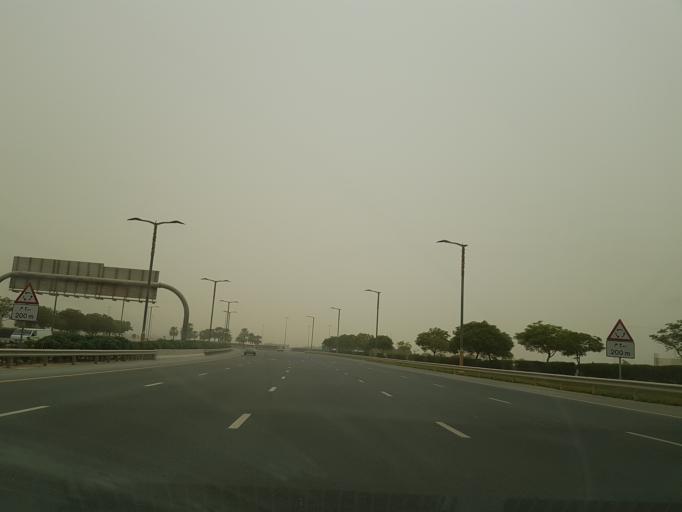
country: AE
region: Dubai
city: Dubai
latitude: 25.1531
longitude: 55.2858
